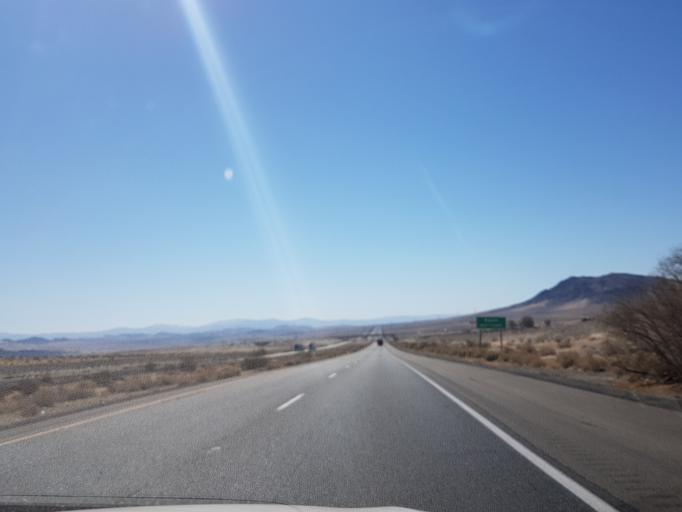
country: US
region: California
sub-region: San Bernardino County
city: Fort Irwin
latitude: 35.0770
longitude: -116.4037
